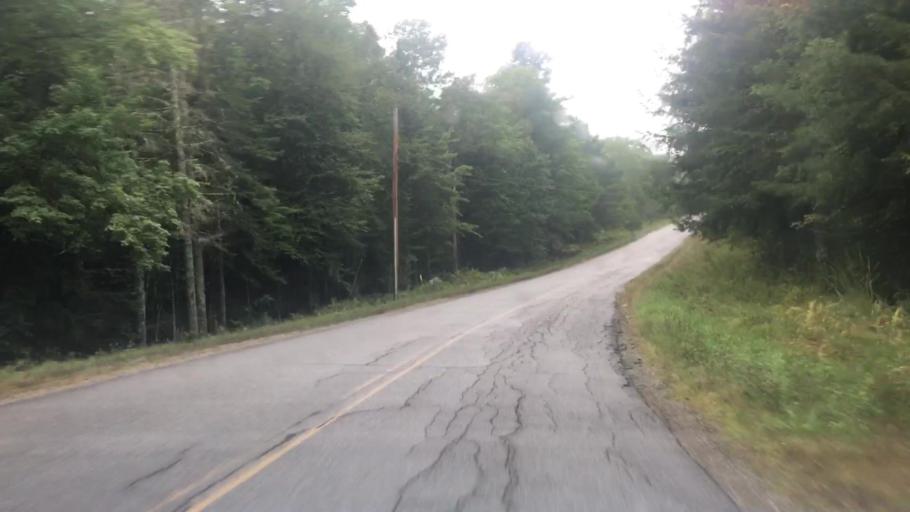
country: US
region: Maine
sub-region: Waldo County
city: Stockton Springs
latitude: 44.5407
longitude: -68.9069
